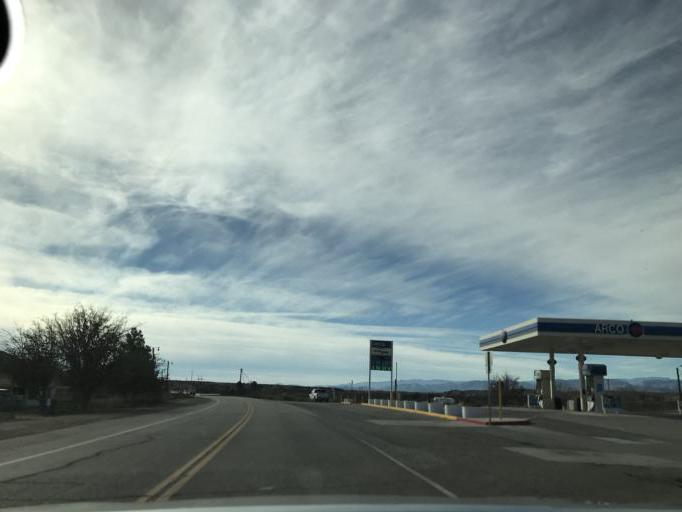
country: US
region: Nevada
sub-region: Clark County
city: Moapa Town
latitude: 36.6653
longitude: -114.5690
